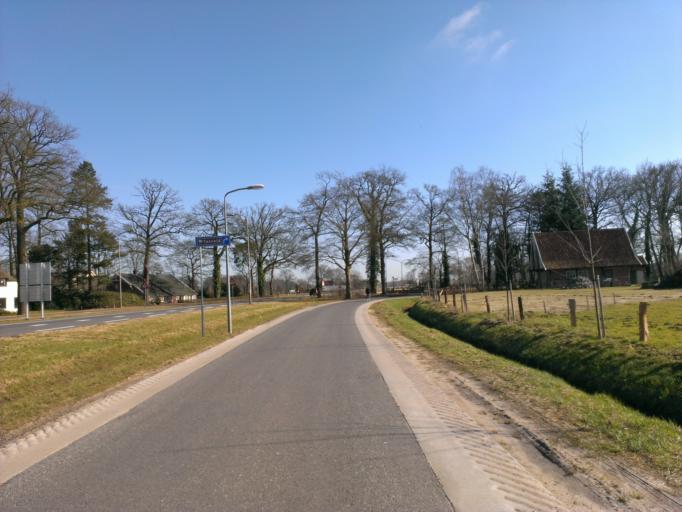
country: NL
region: Overijssel
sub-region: Gemeente Almelo
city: Almelo
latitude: 52.3365
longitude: 6.6996
